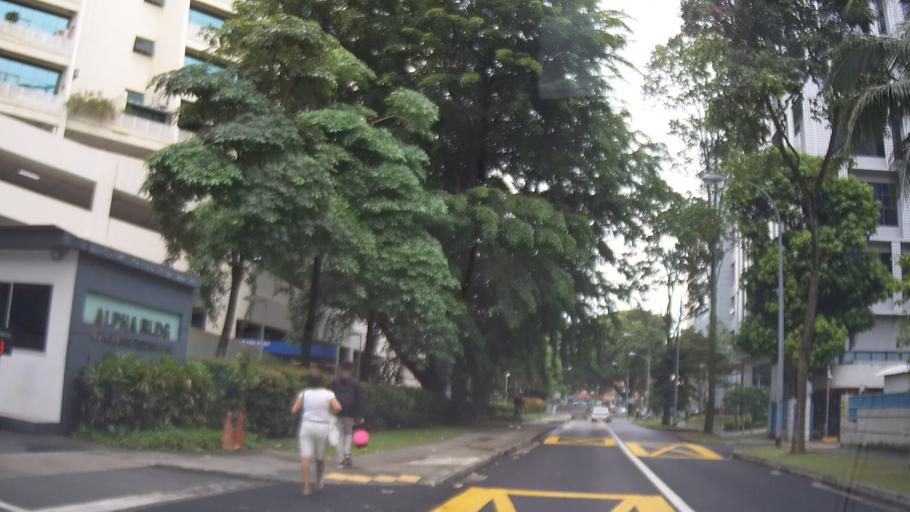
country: SG
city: Singapore
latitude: 1.3288
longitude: 103.8787
